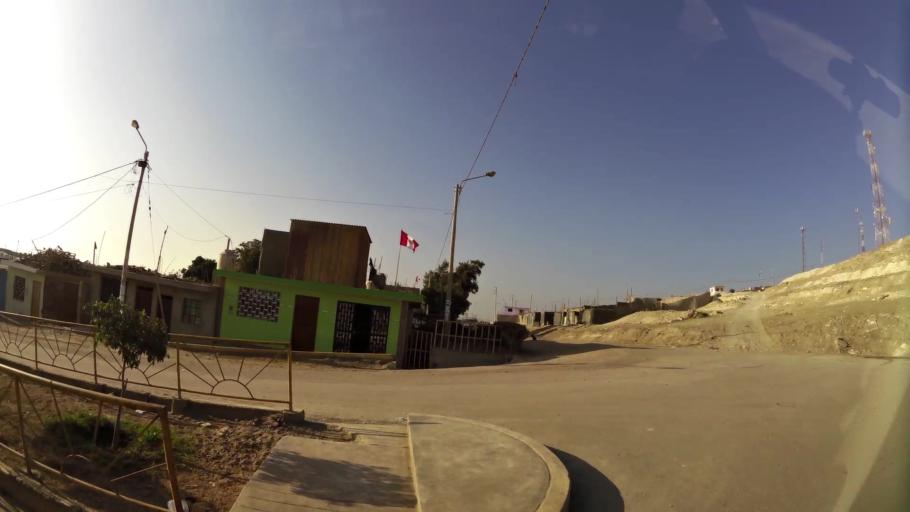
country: PE
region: Ica
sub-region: Provincia de Pisco
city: Villa Tupac Amaru
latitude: -13.7146
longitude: -76.1465
